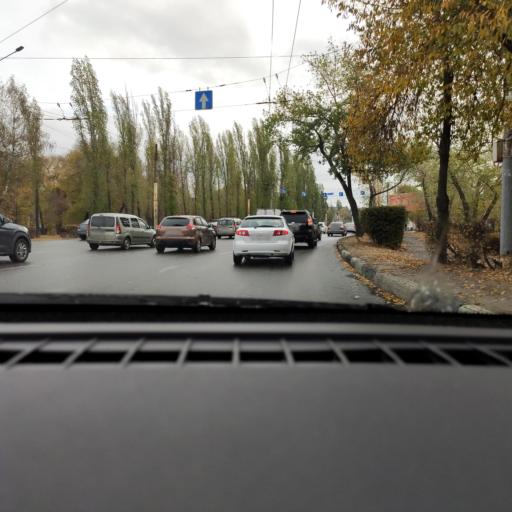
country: RU
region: Voronezj
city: Voronezh
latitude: 51.6323
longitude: 39.2289
